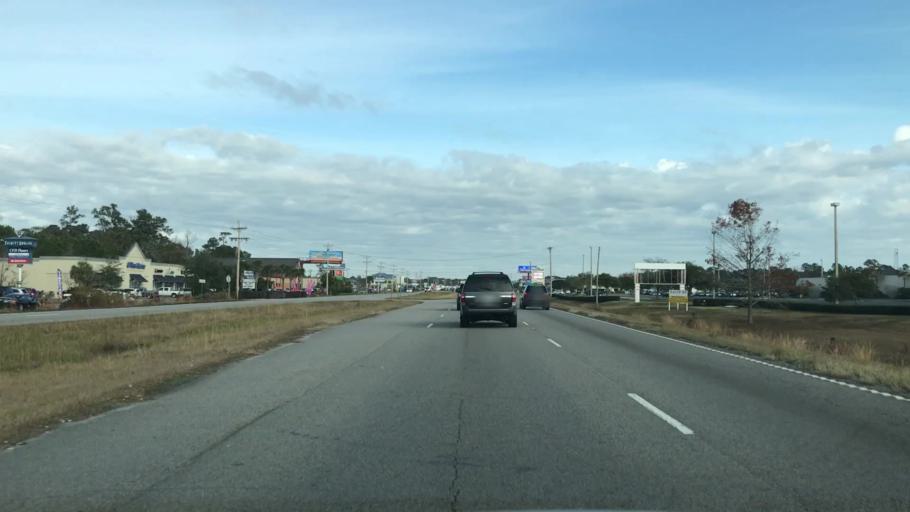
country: US
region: South Carolina
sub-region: Horry County
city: Garden City
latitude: 33.5790
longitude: -79.0285
